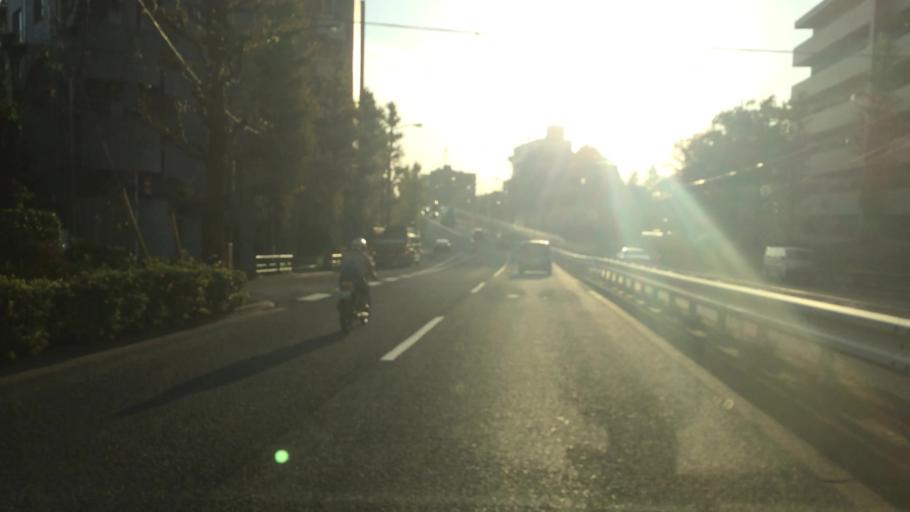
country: JP
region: Tokyo
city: Tokyo
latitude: 35.6103
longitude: 139.6513
